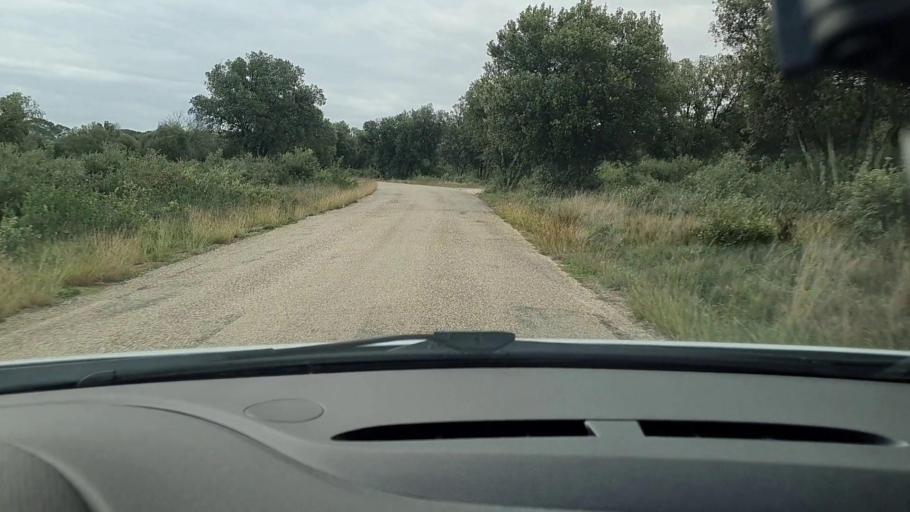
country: FR
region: Languedoc-Roussillon
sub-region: Departement du Gard
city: Salindres
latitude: 44.1660
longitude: 4.2462
